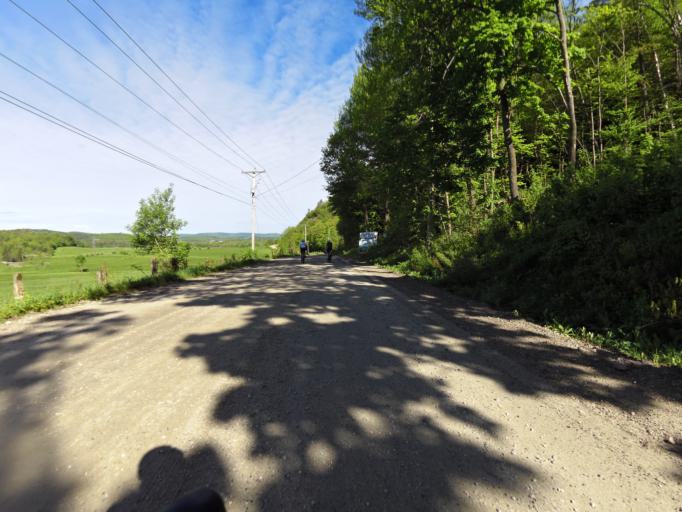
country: CA
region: Quebec
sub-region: Outaouais
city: Wakefield
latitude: 45.6755
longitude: -75.8774
